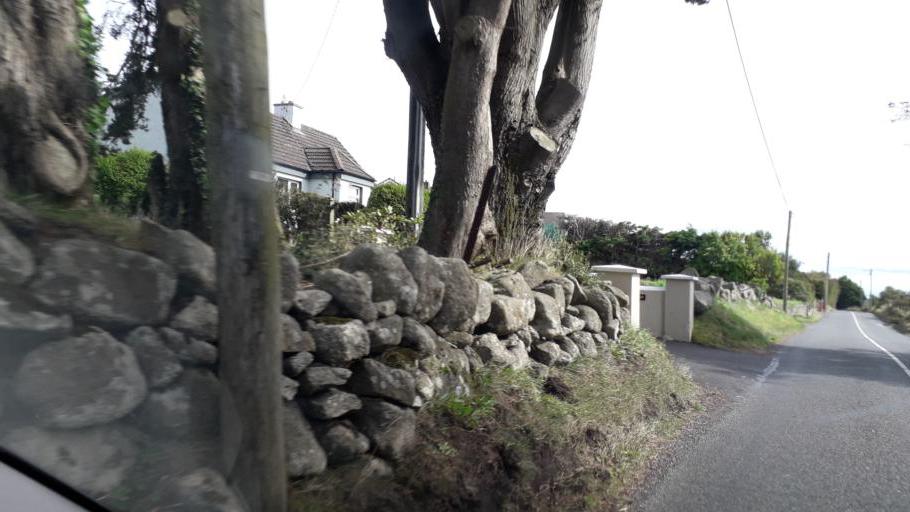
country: IE
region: Leinster
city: Balally
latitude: 53.2216
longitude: -6.2343
